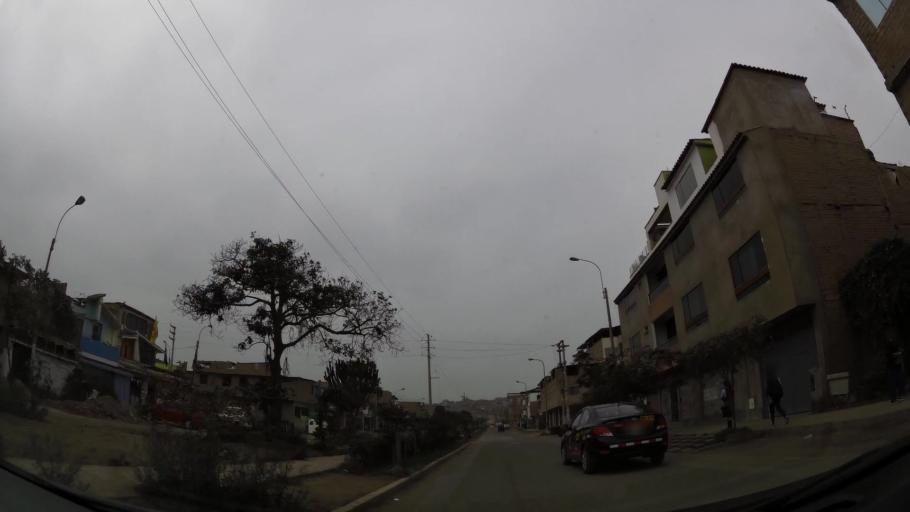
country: PE
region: Lima
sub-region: Lima
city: Surco
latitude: -12.2348
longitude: -76.9209
